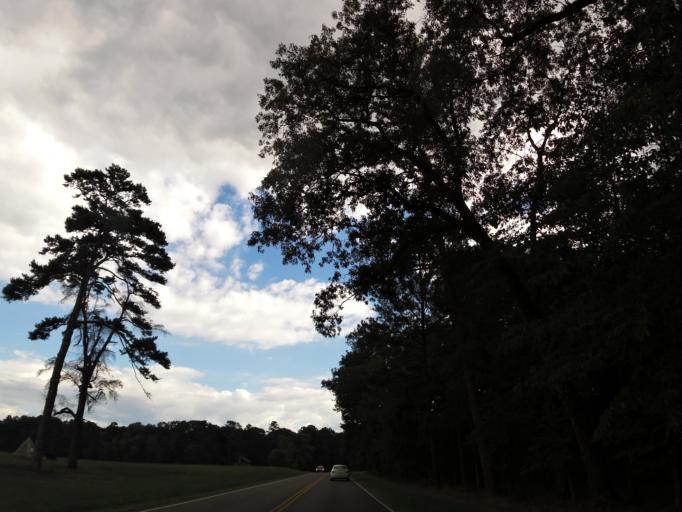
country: US
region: Georgia
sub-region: Catoosa County
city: Fort Oglethorpe
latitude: 34.9304
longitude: -85.2598
